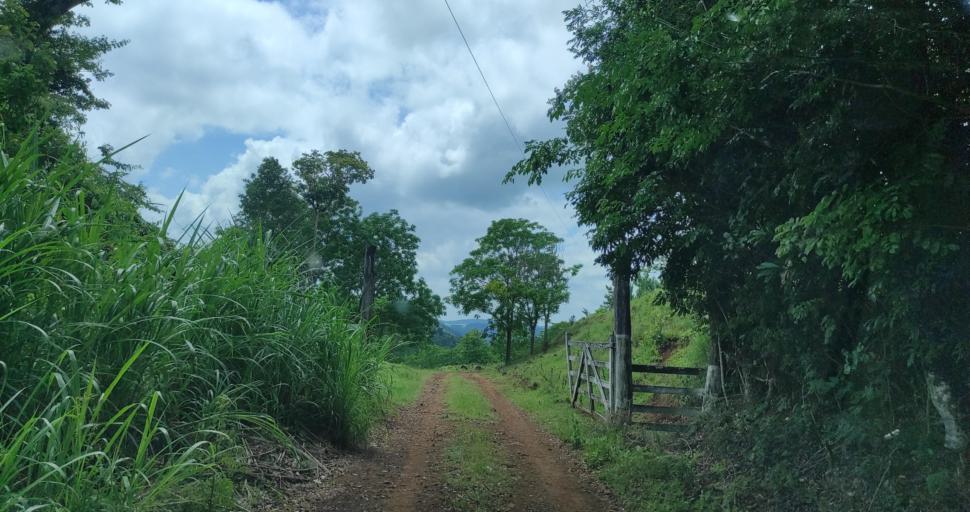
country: AR
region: Misiones
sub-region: Departamento de Veinticinco de Mayo
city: Veinticinco de Mayo
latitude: -27.4162
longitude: -54.7214
